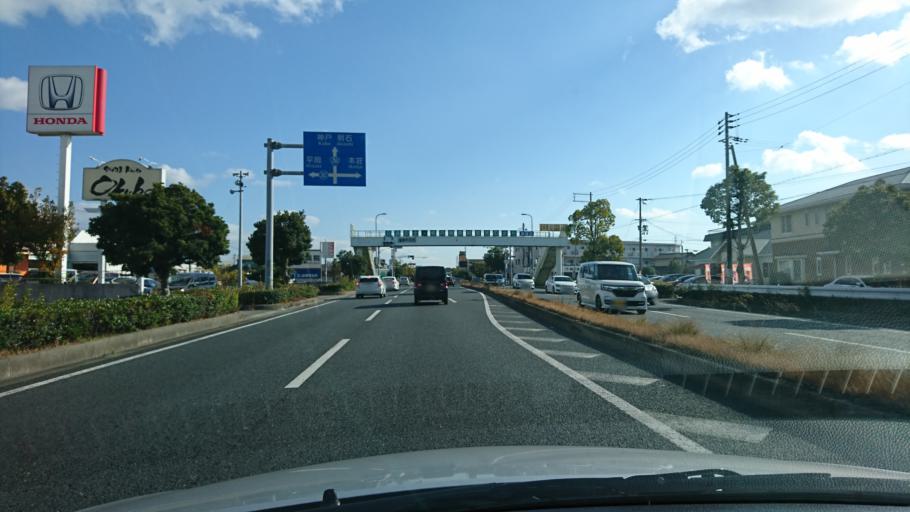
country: JP
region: Hyogo
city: Kakogawacho-honmachi
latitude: 34.7261
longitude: 134.8654
